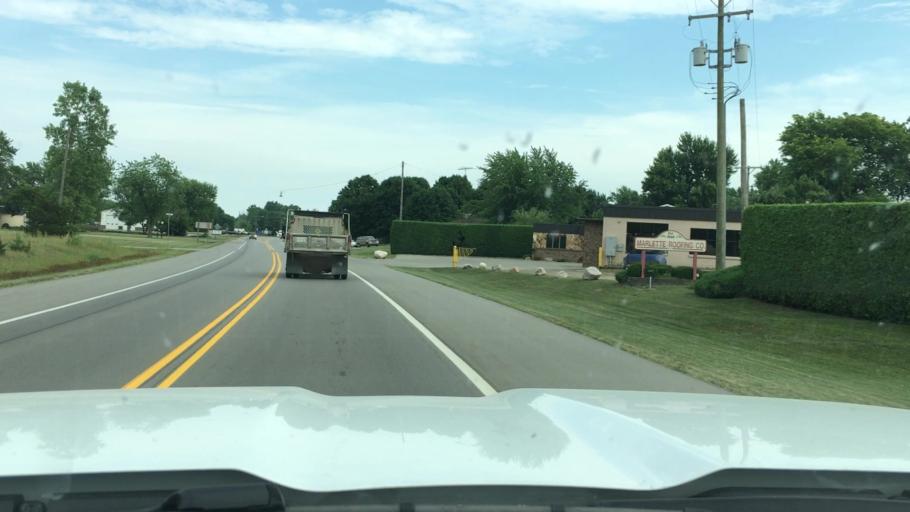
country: US
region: Michigan
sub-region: Sanilac County
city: Marlette
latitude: 43.3373
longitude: -83.0833
